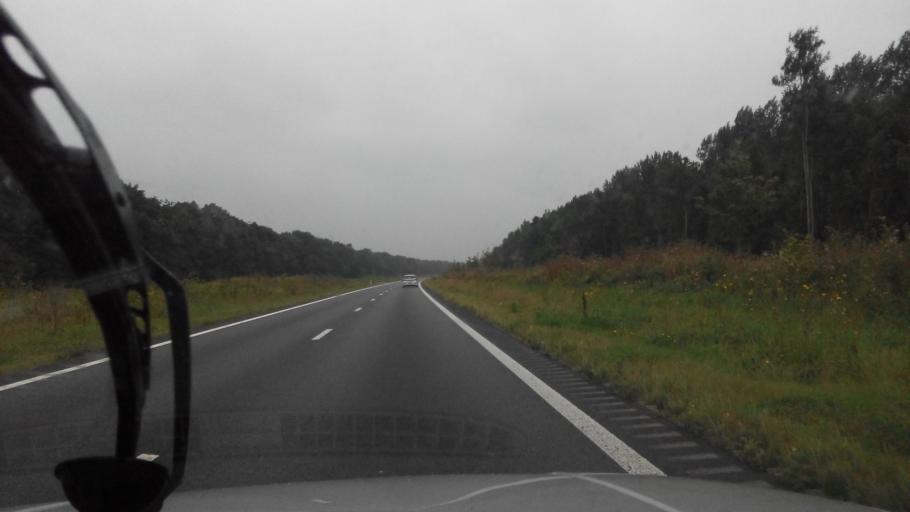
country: NL
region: Flevoland
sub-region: Gemeente Zeewolde
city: Zeewolde
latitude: 52.3380
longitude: 5.4849
